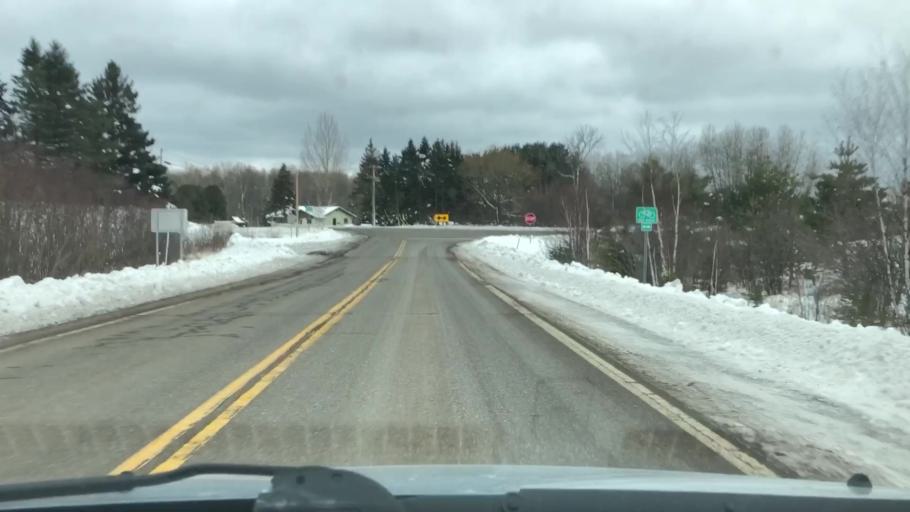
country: US
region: Minnesota
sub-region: Saint Louis County
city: Proctor
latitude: 46.7074
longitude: -92.2775
